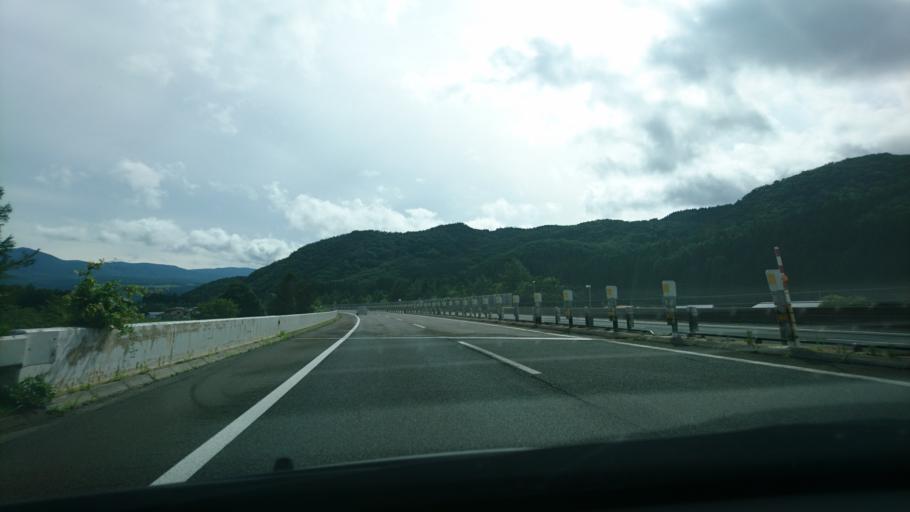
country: JP
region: Akita
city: Hanawa
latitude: 40.0456
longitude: 140.9981
